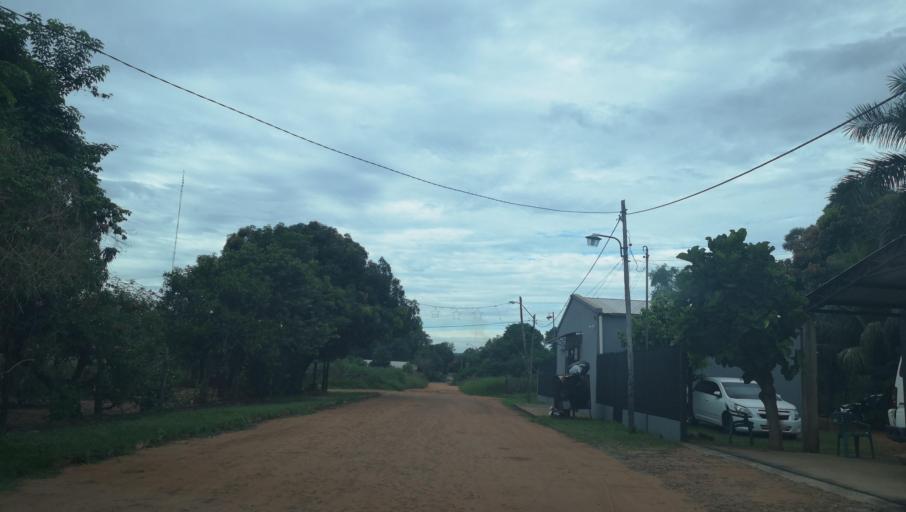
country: PY
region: San Pedro
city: Capiibary
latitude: -24.7336
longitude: -56.0227
